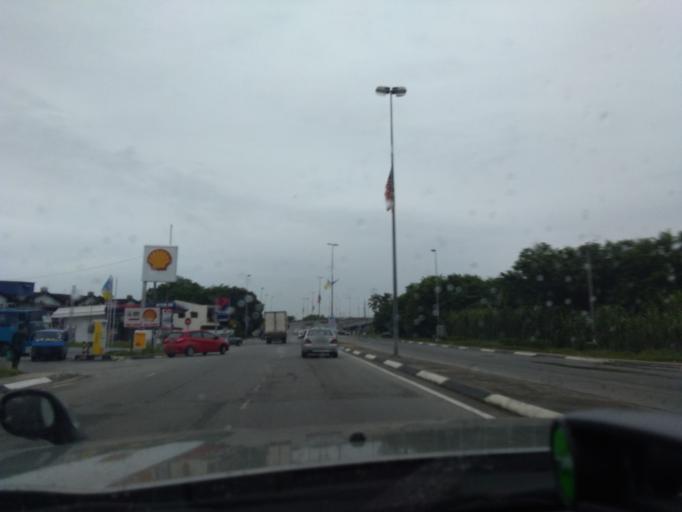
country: MY
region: Penang
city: Nibong Tebal
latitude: 5.1679
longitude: 100.4788
